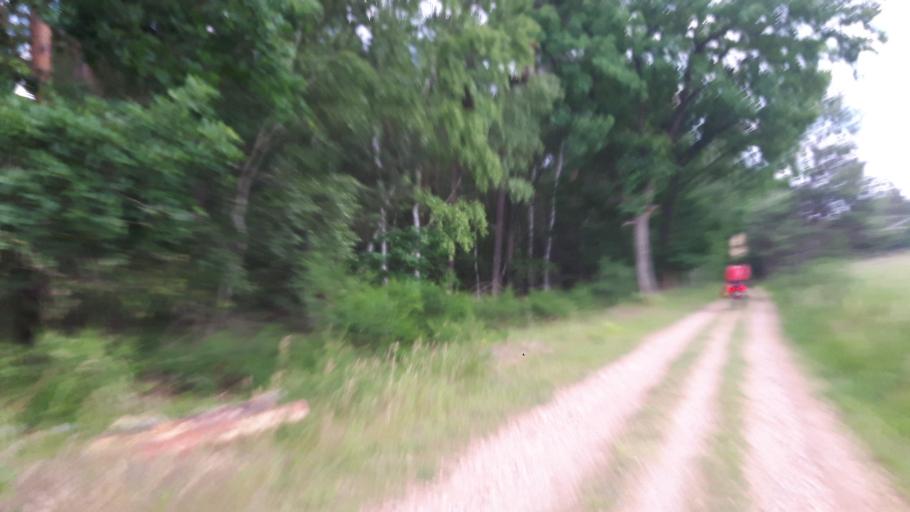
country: DE
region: Saxony-Anhalt
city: Radis
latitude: 51.7788
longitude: 12.5393
